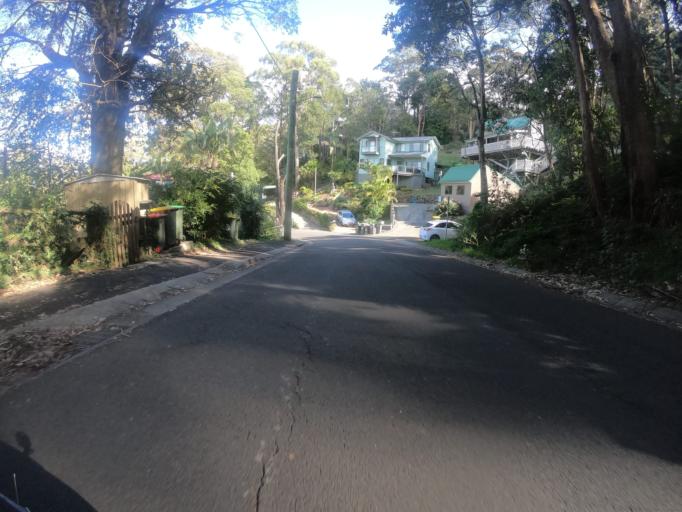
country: AU
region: New South Wales
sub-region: Wollongong
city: Bulli
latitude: -34.3044
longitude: 150.9257
